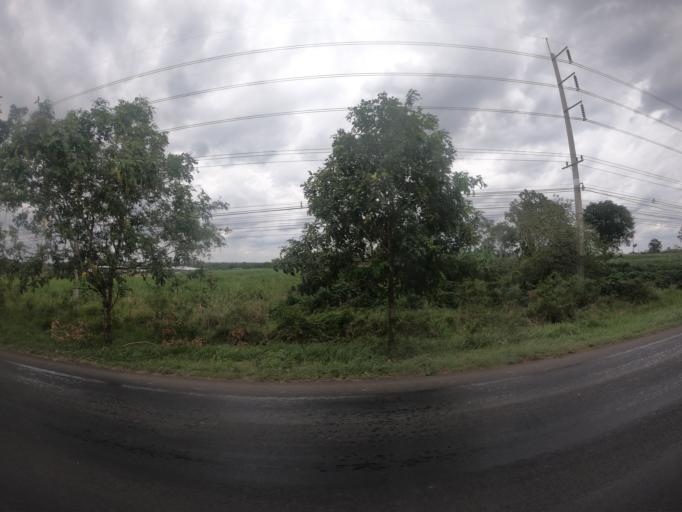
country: TH
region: Nakhon Ratchasima
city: Nong Bun Nak
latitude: 14.7591
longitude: 102.3103
